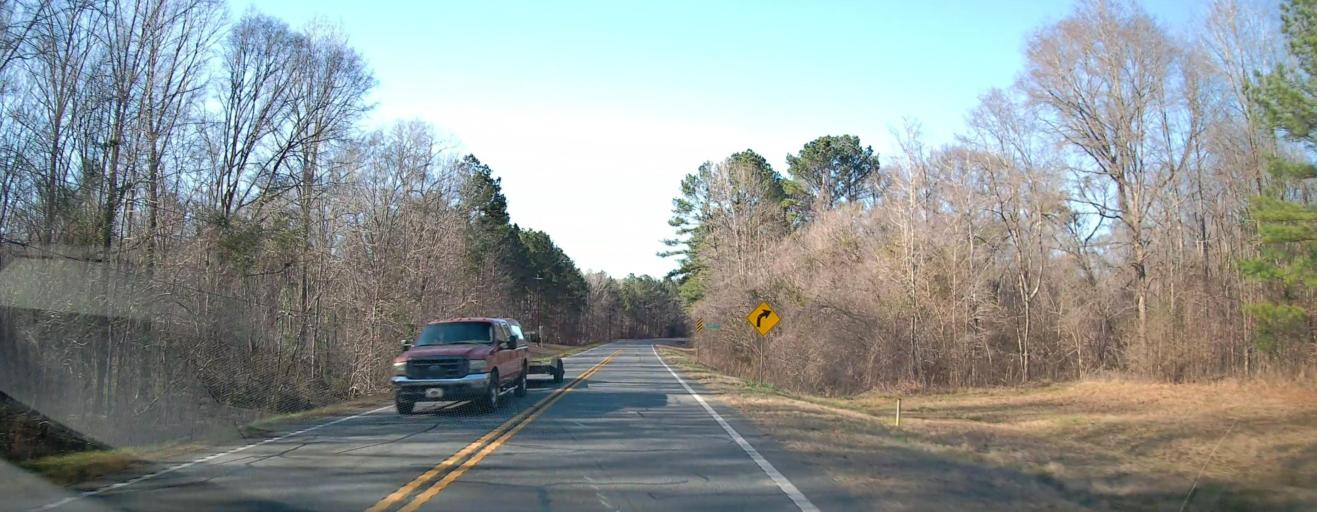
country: US
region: Georgia
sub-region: Talbot County
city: Talbotton
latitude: 32.7078
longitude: -84.5552
